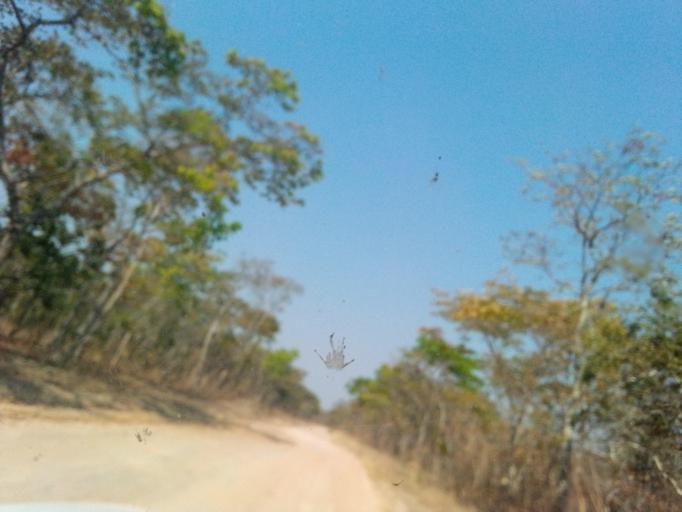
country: ZM
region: Northern
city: Mpika
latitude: -12.2270
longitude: 30.8906
